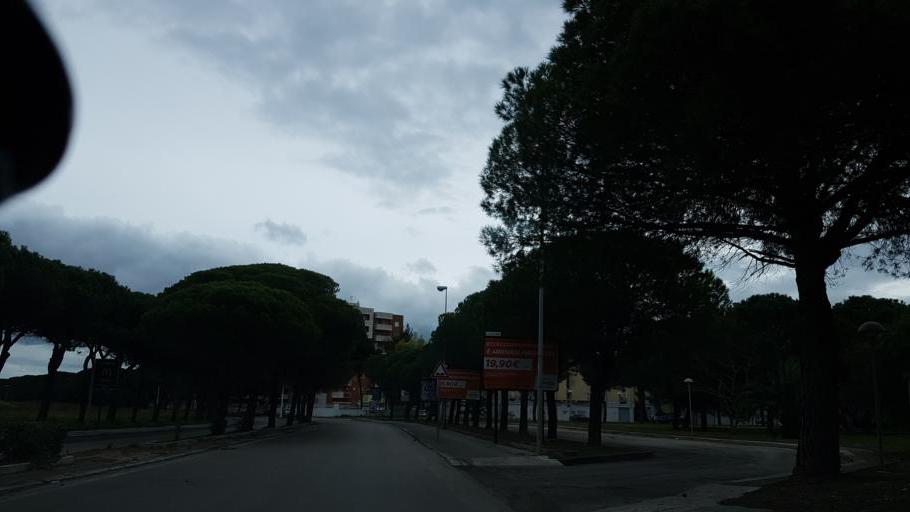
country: IT
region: Apulia
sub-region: Provincia di Brindisi
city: Brindisi
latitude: 40.6213
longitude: 17.9197
